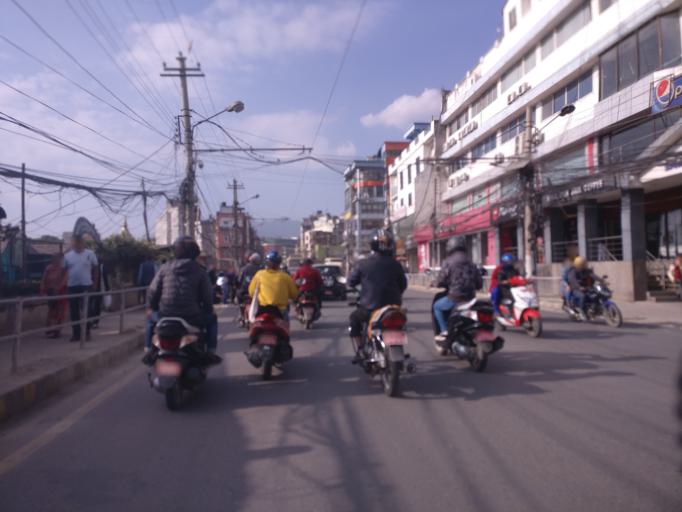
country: NP
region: Central Region
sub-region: Bagmati Zone
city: Kathmandu
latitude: 27.6912
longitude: 85.3167
